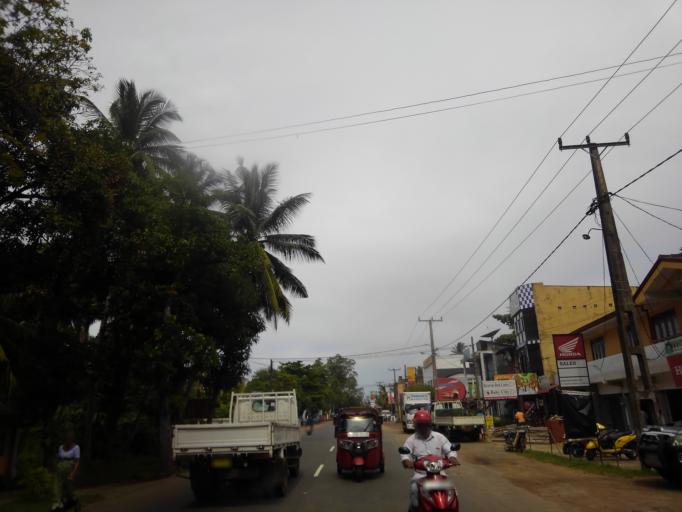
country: LK
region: Western
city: Beruwala
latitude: 6.4719
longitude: 79.9847
